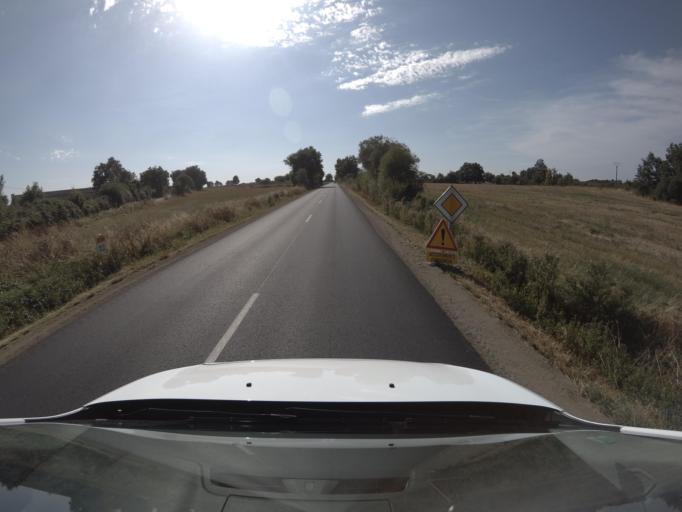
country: FR
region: Poitou-Charentes
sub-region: Departement des Deux-Sevres
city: Mauze-Thouarsais
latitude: 46.9992
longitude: -0.3147
